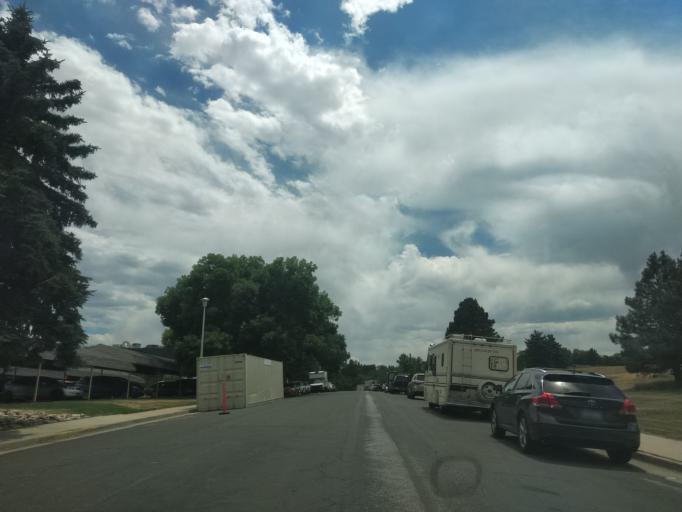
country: US
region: Colorado
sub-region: Jefferson County
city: Lakewood
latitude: 39.6902
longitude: -105.1224
